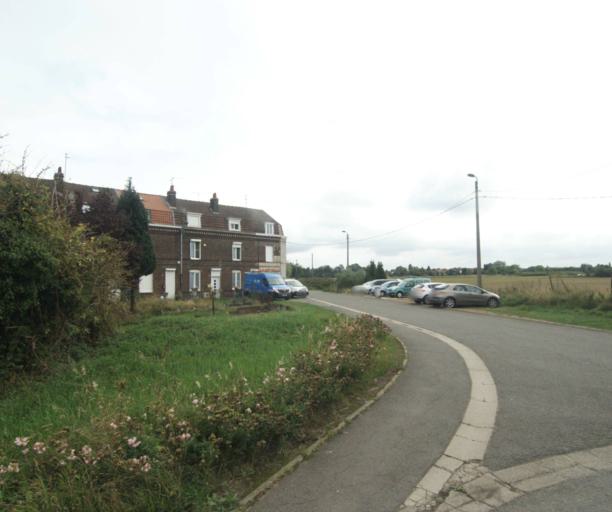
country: FR
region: Nord-Pas-de-Calais
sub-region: Departement du Nord
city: Lezennes
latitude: 50.6222
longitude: 3.1134
